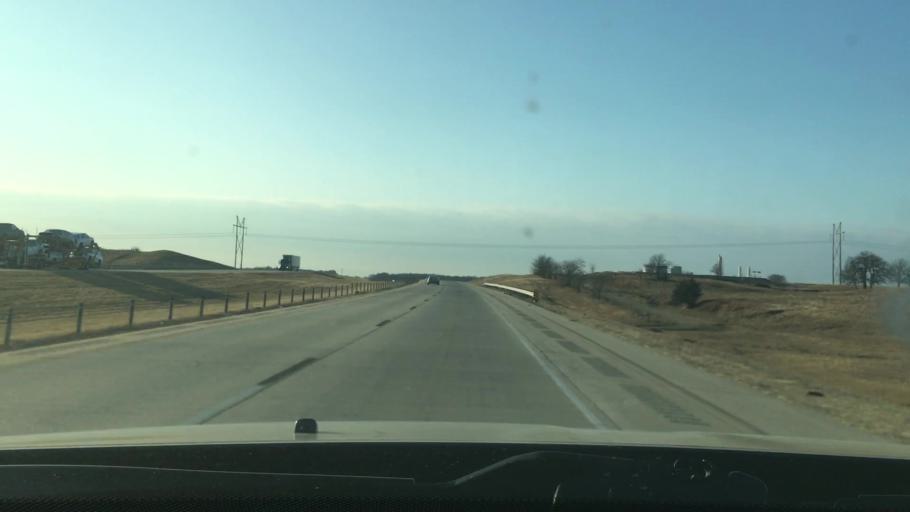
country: US
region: Oklahoma
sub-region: Carter County
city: Ardmore
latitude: 34.2558
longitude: -97.1653
